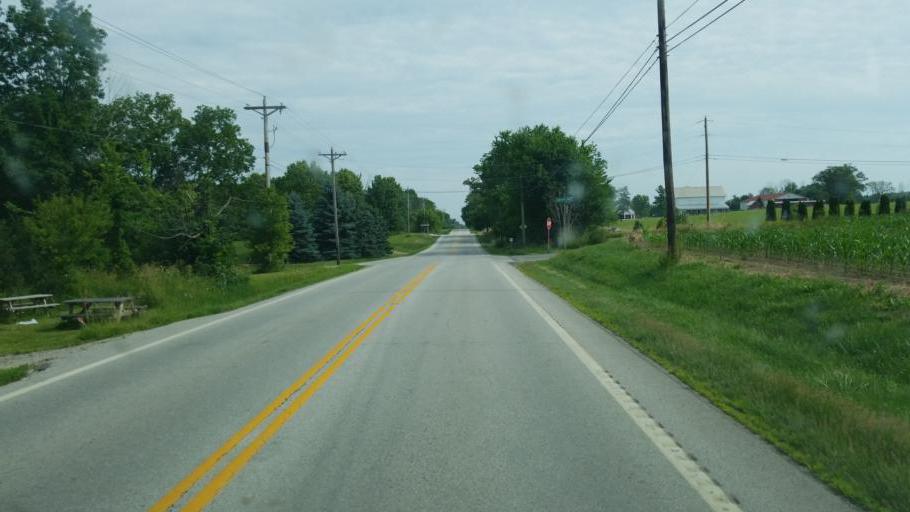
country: US
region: Ohio
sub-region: Medina County
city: Lodi
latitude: 41.1120
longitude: -82.0242
